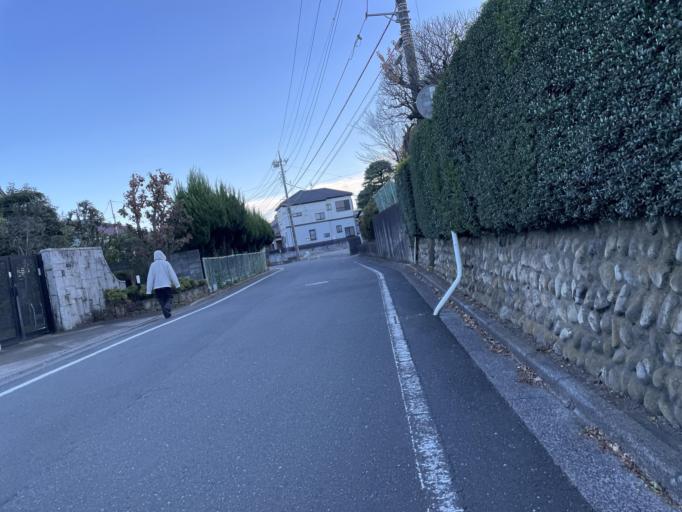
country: JP
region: Saitama
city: Wako
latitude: 35.7952
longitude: 139.6239
